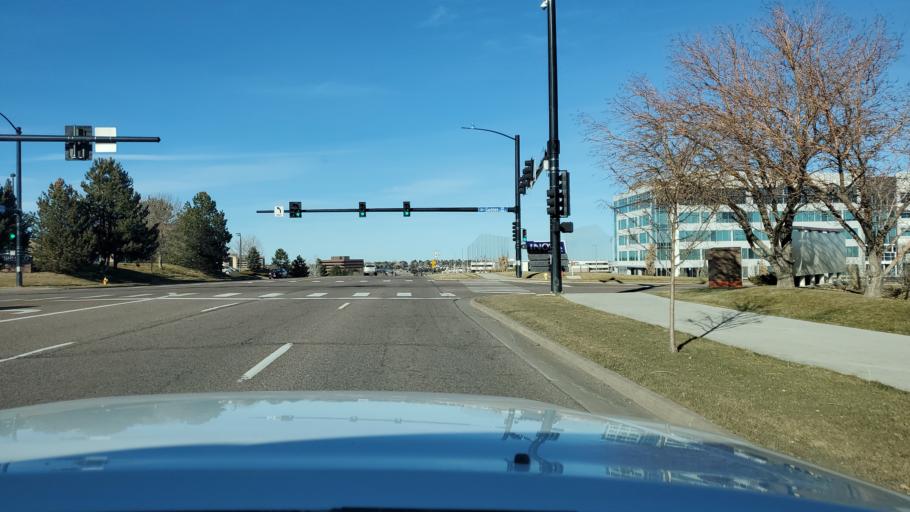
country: US
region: Colorado
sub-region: Arapahoe County
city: Centennial
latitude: 39.5838
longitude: -104.8667
